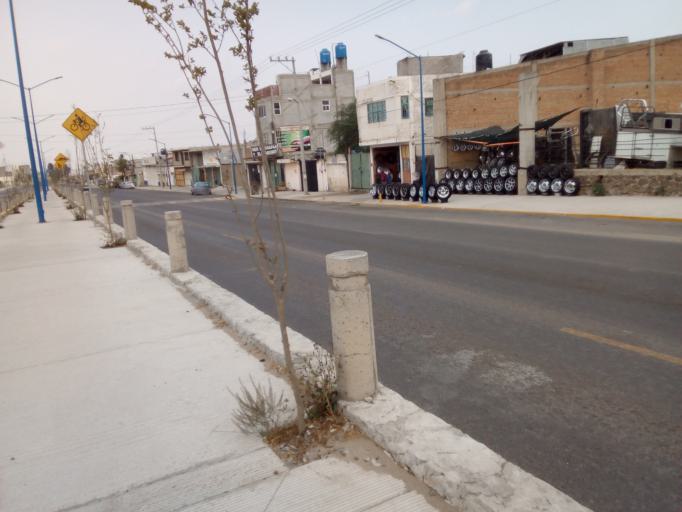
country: MX
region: Guerrero
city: San Luis de la Paz
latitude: 21.2883
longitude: -100.5161
